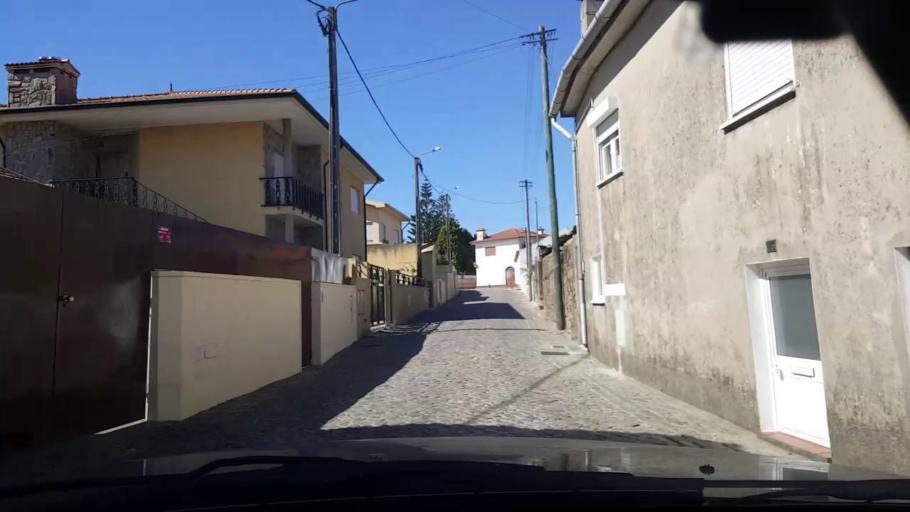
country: PT
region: Porto
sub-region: Matosinhos
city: Lavra
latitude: 41.2960
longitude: -8.6890
